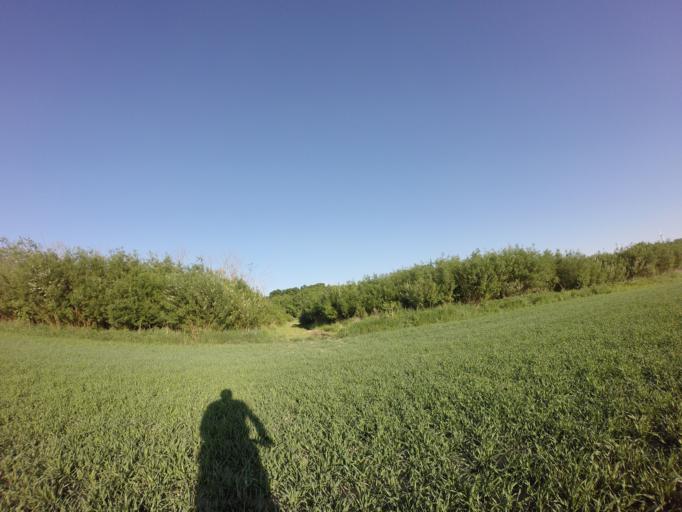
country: PL
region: West Pomeranian Voivodeship
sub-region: Powiat choszczenski
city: Choszczno
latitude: 53.1329
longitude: 15.4327
